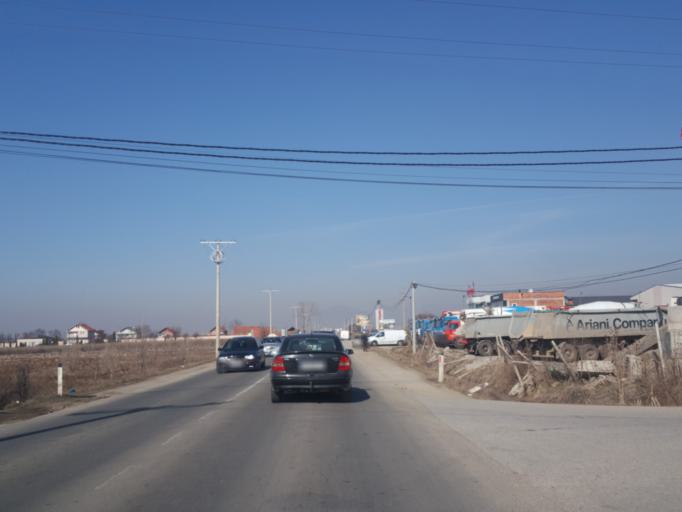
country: XK
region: Mitrovica
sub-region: Vushtrri
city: Vushtrri
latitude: 42.7996
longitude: 20.9962
